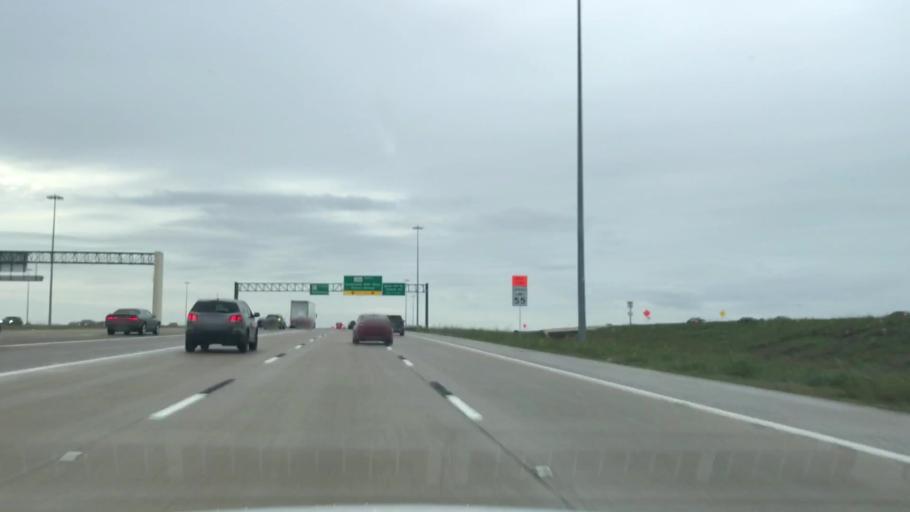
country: US
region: Texas
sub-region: Dallas County
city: Coppell
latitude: 32.9403
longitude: -97.0399
